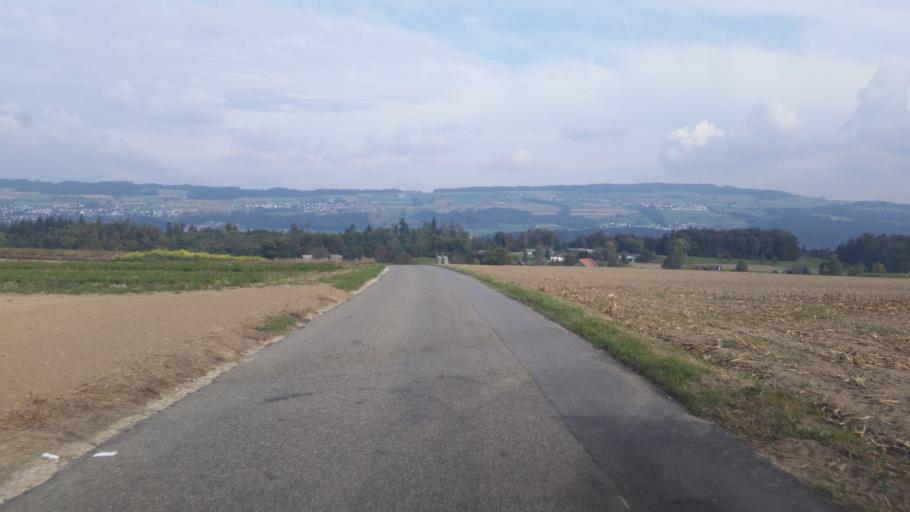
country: CH
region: Aargau
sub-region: Bezirk Bremgarten
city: Hagglingen
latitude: 47.3903
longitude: 8.2686
